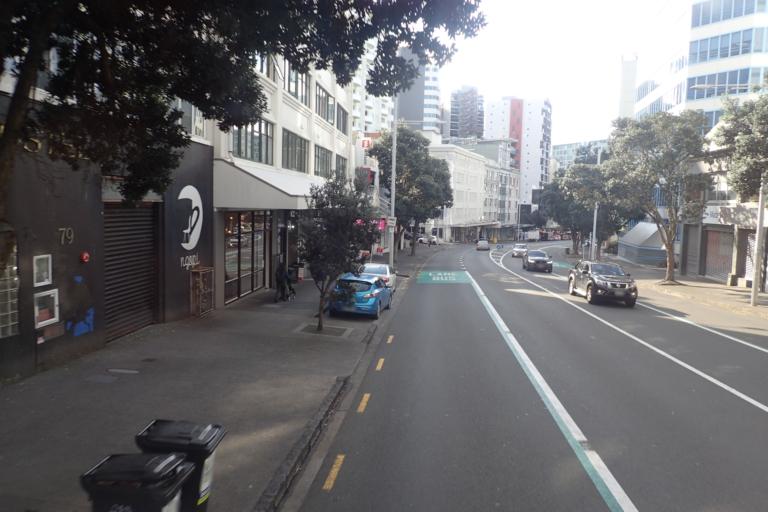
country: NZ
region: Auckland
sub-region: Auckland
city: Auckland
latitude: -36.8478
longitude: 174.7727
